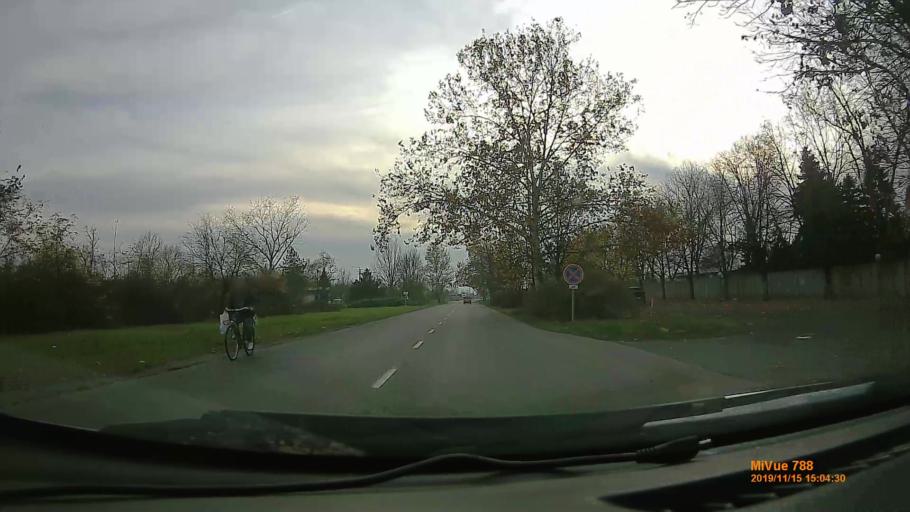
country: HU
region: Bekes
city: Gyula
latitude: 46.6372
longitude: 21.2611
